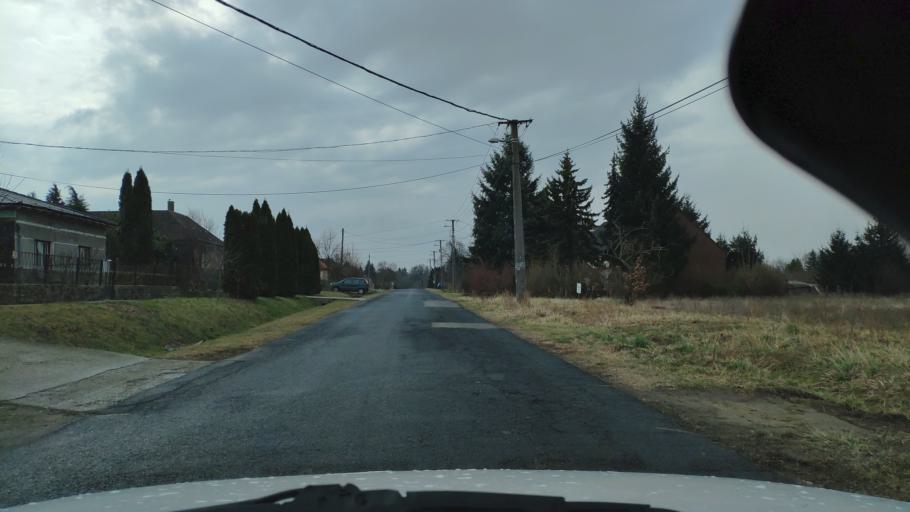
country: HU
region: Zala
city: Nagykanizsa
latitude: 46.4144
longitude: 16.9982
